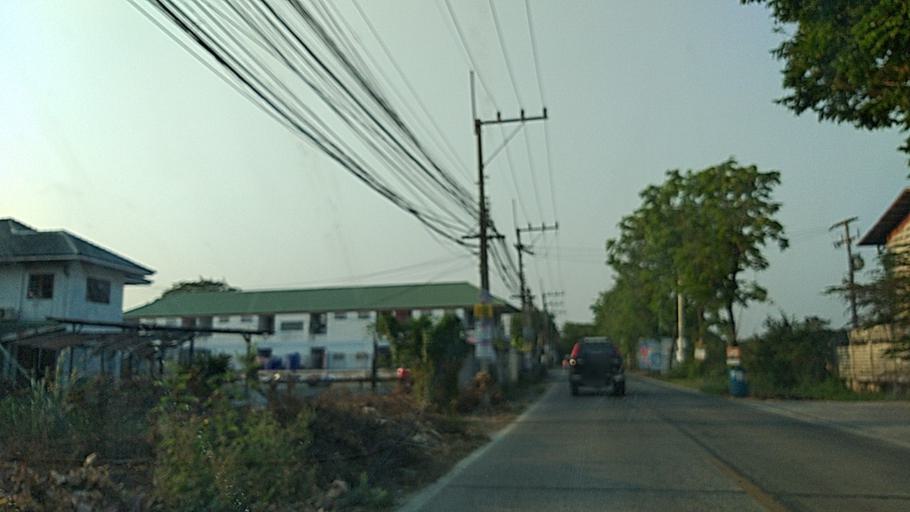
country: TH
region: Phra Nakhon Si Ayutthaya
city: Ban Bang Kadi Pathum Thani
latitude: 13.9971
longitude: 100.5643
